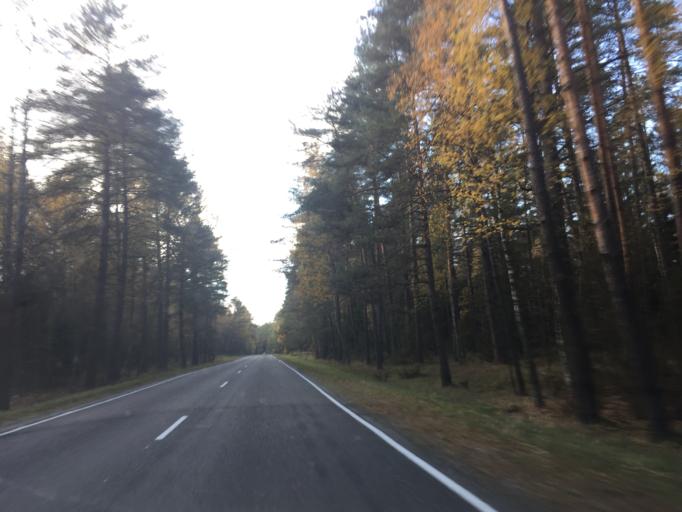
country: BY
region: Minsk
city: Narach
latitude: 54.9558
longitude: 26.6080
